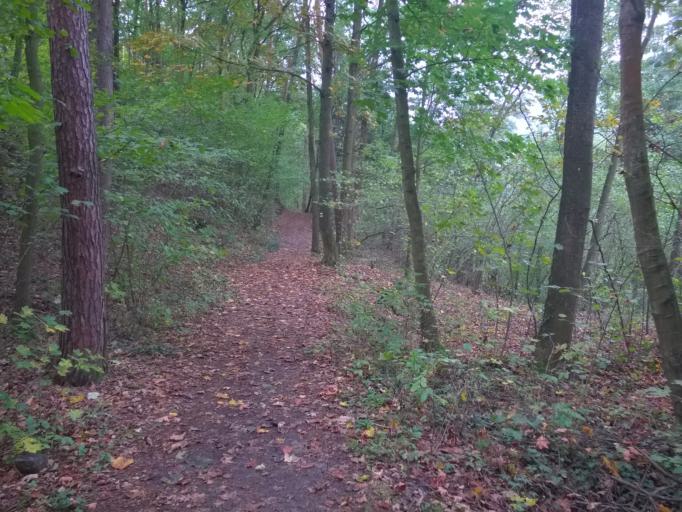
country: CZ
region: Central Bohemia
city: Kamenny Privoz
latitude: 49.8703
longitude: 14.4886
